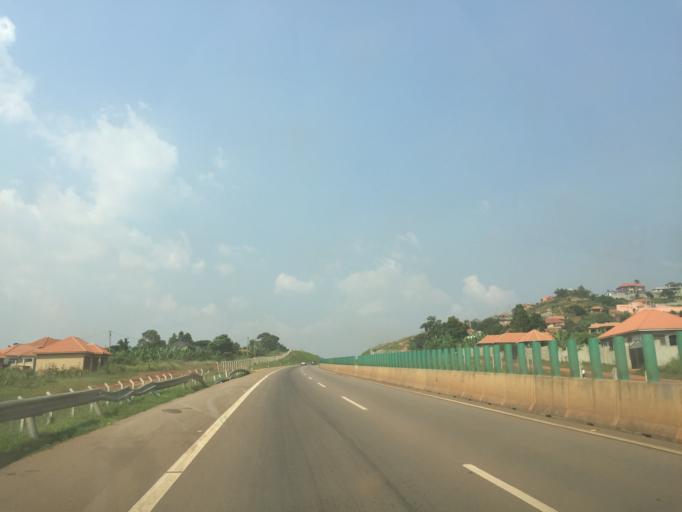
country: UG
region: Central Region
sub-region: Wakiso District
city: Kajansi
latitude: 0.1700
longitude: 32.5147
